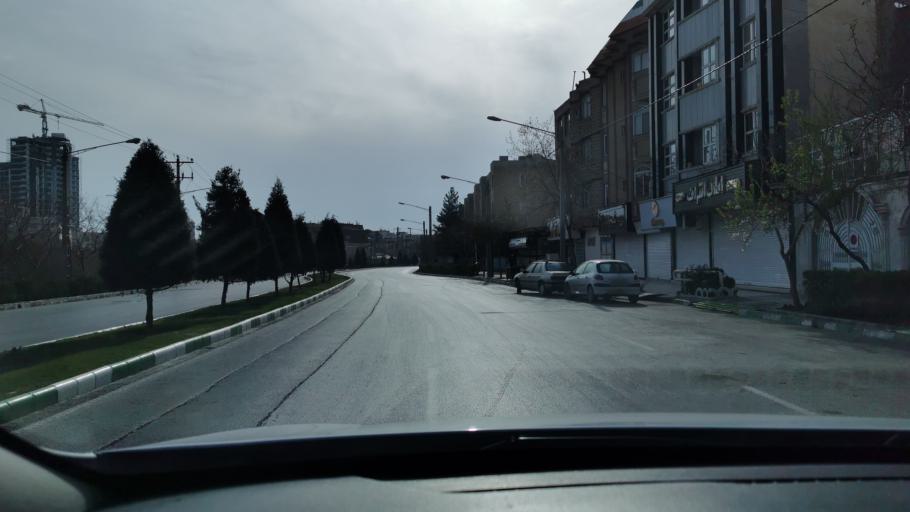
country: IR
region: Razavi Khorasan
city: Mashhad
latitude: 36.3138
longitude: 59.5125
